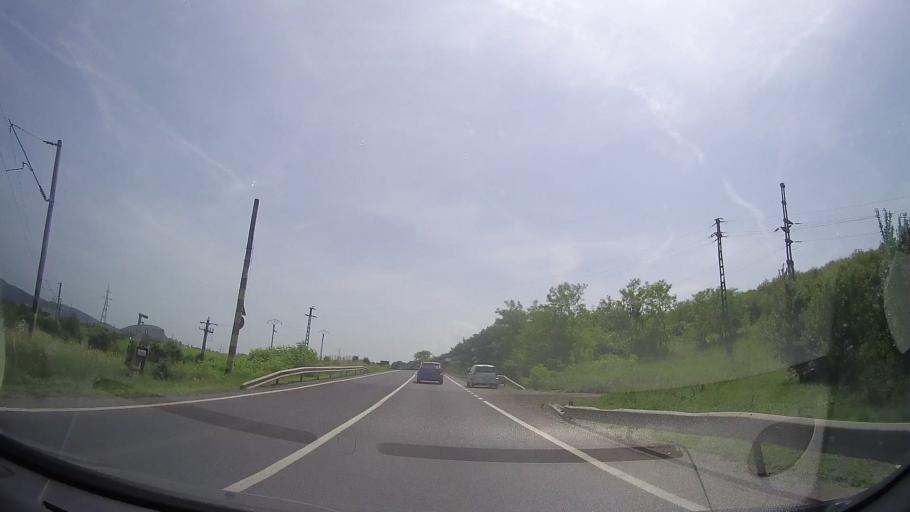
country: RO
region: Hunedoara
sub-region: Oras Simeria
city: Simeria
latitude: 45.8496
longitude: 22.9813
